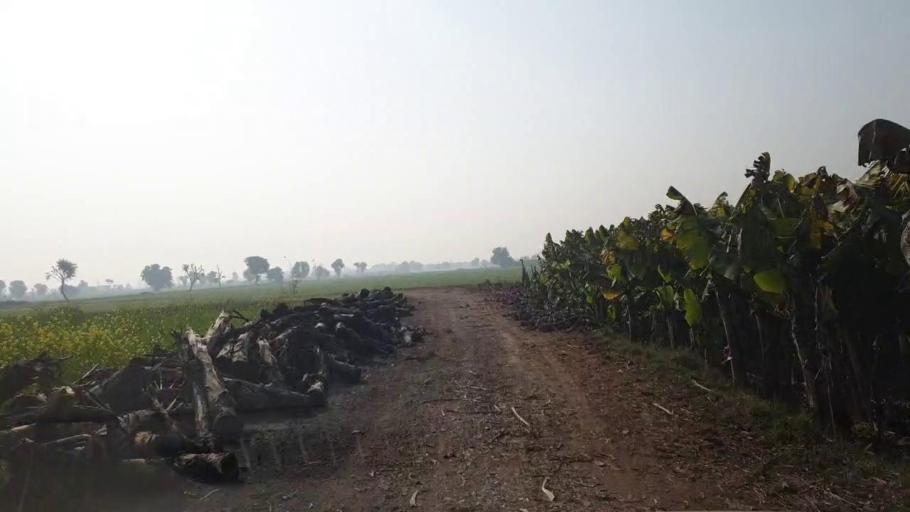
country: PK
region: Sindh
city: Sakrand
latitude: 26.0046
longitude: 68.3634
